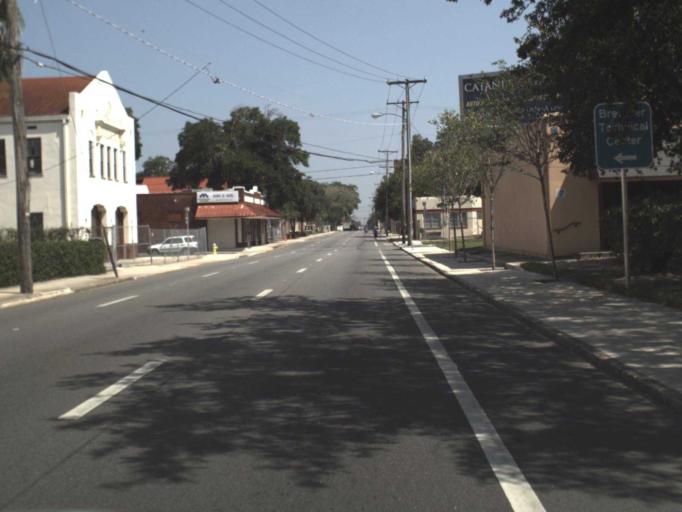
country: US
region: Florida
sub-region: Hillsborough County
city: Tampa
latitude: 27.9625
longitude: -82.4595
